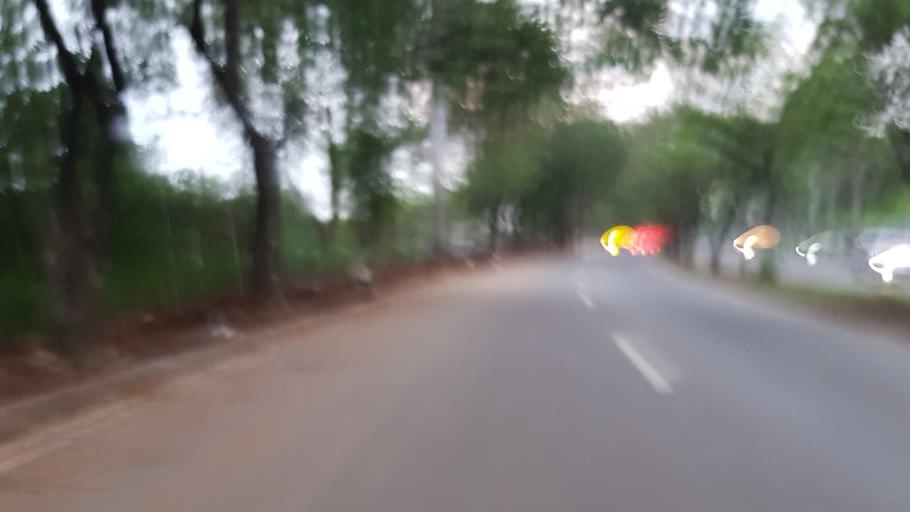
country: ID
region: West Java
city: Ciputat
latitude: -6.1911
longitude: 106.7359
